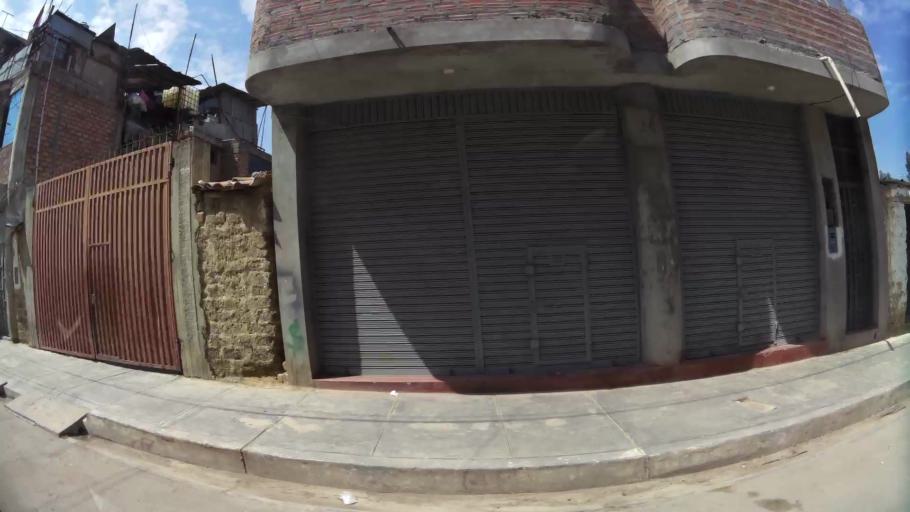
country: PE
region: Junin
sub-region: Provincia de Huancayo
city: El Tambo
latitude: -12.0752
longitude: -75.2158
